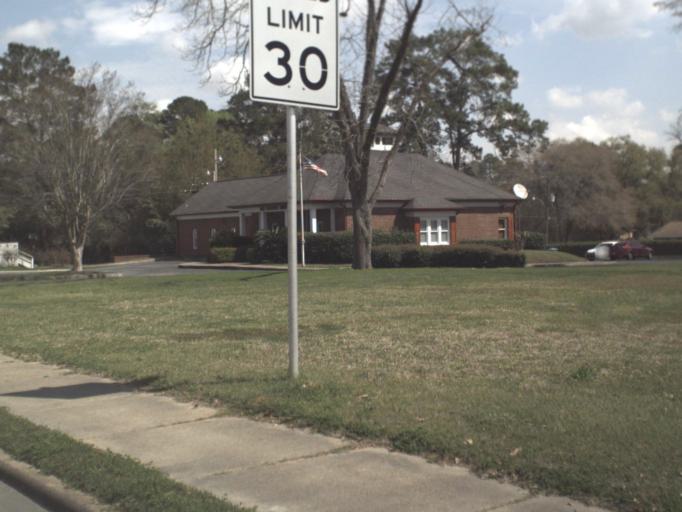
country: US
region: Florida
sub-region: Gadsden County
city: Havana
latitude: 30.6216
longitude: -84.4152
